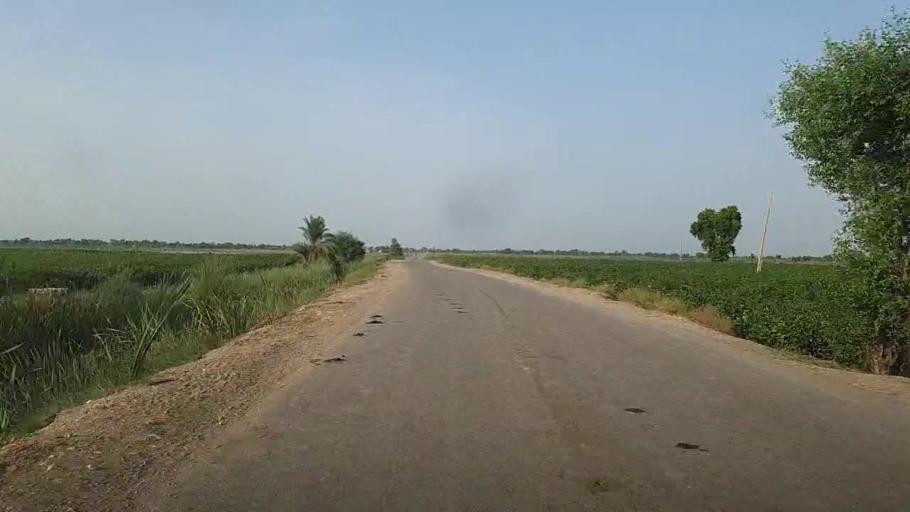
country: PK
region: Sindh
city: Khairpur
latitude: 28.0882
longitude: 69.8022
